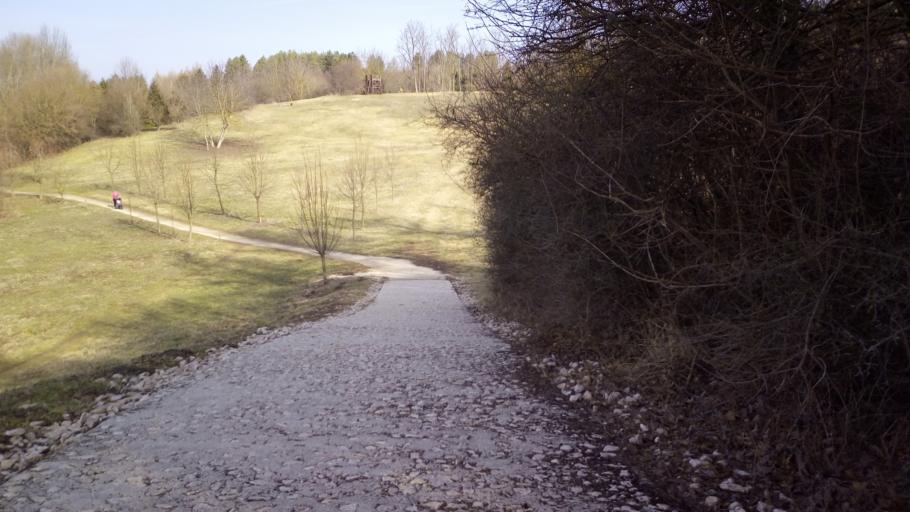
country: HU
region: Baranya
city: Pellerd
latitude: 46.0087
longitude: 18.2029
